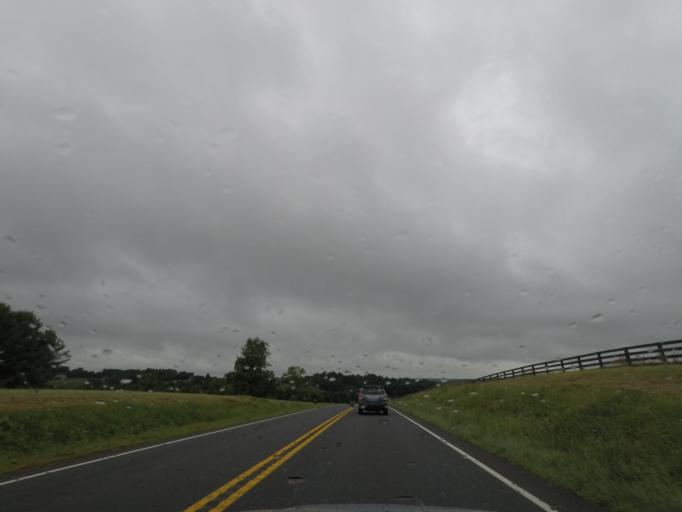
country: US
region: Virginia
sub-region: Orange County
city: Orange
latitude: 38.2698
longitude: -78.1259
